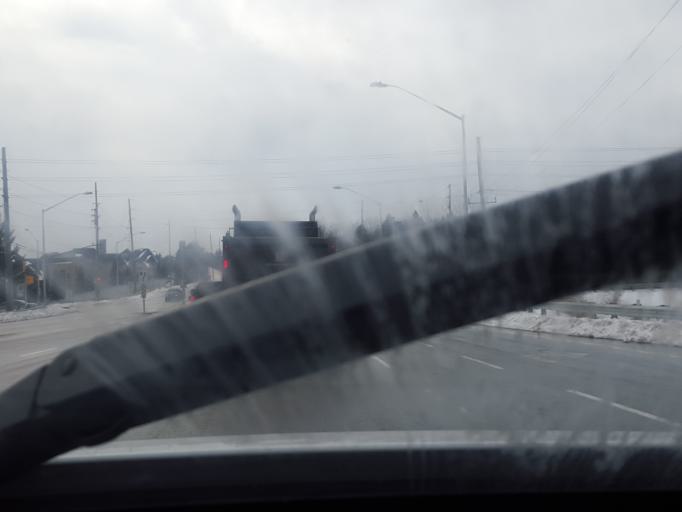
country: CA
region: Ontario
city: Newmarket
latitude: 43.9683
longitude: -79.4339
